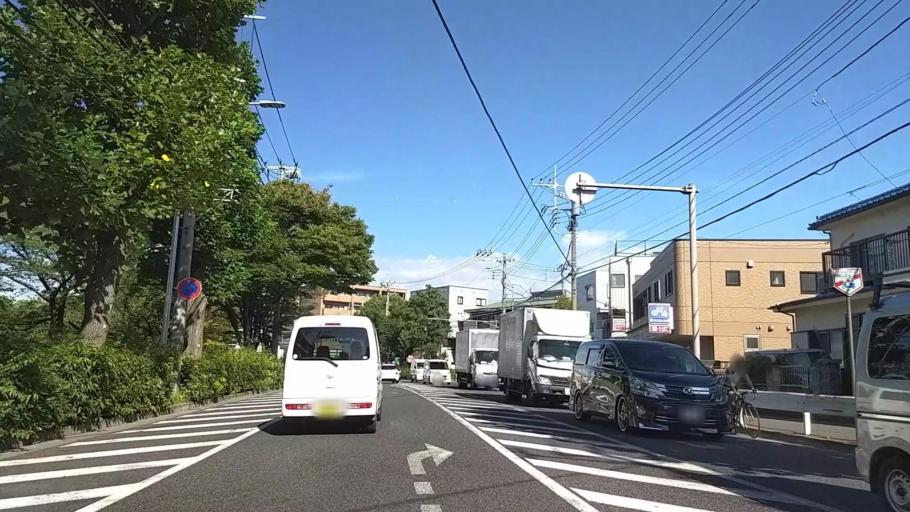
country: JP
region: Kanagawa
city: Yokohama
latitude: 35.4960
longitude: 139.6182
